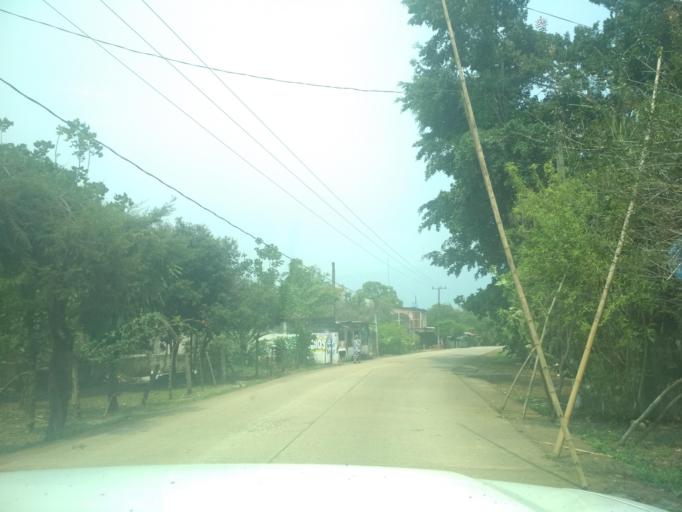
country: MX
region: Veracruz
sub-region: Tezonapa
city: Laguna Chica (Pueblo Nuevo)
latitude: 18.5158
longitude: -96.7765
